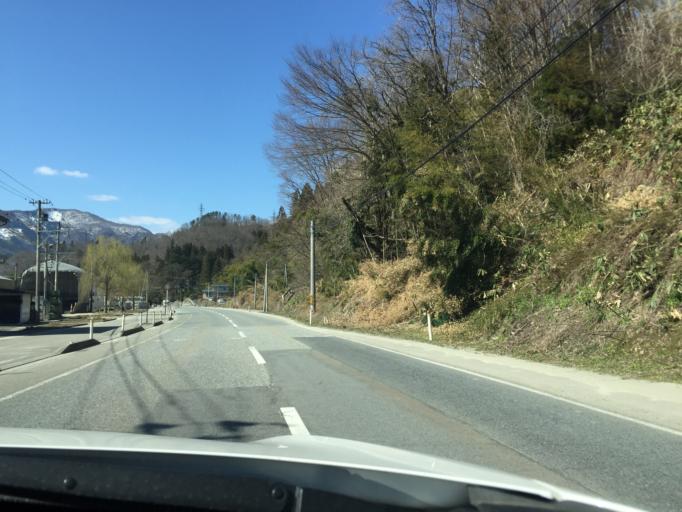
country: JP
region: Yamagata
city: Nagai
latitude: 38.2227
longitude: 140.0985
